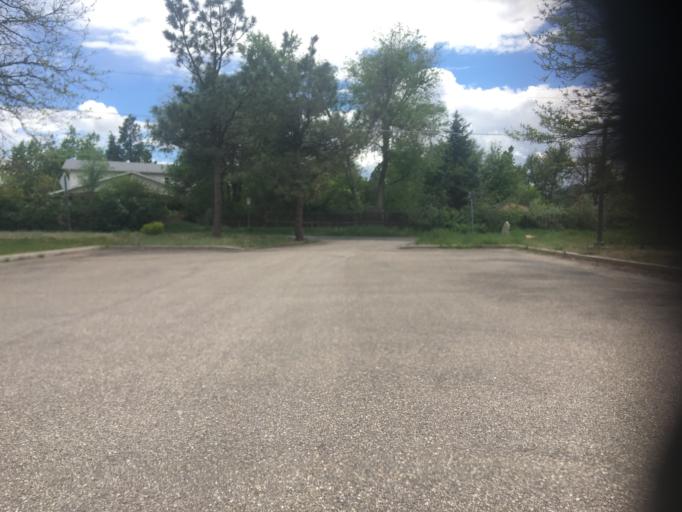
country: US
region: Colorado
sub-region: Boulder County
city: Boulder
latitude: 40.0069
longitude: -105.2332
